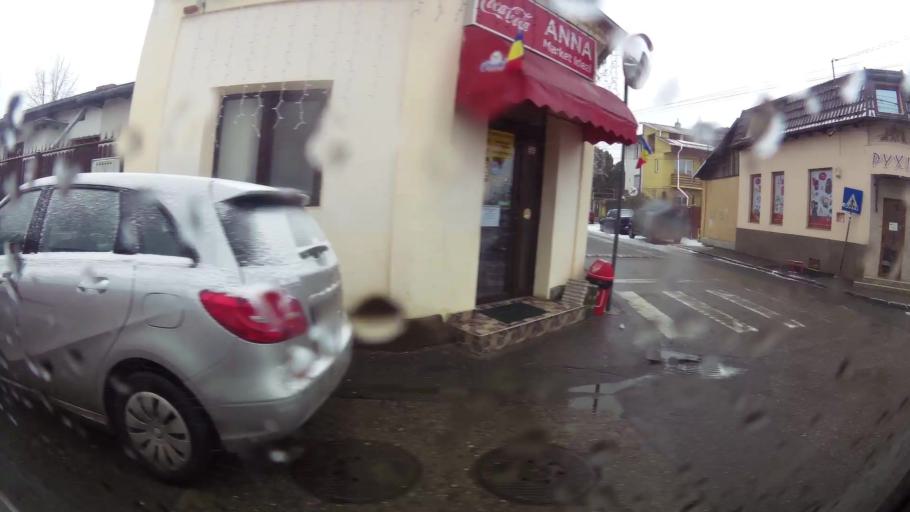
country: RO
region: Prahova
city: Ploiesti
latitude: 44.9438
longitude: 26.0110
